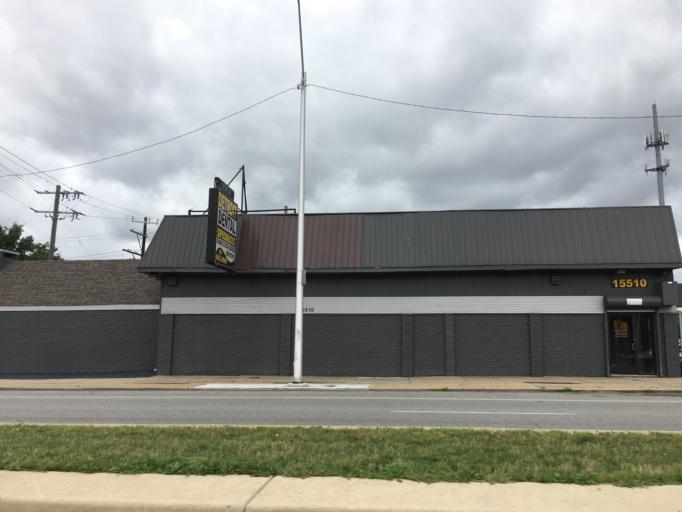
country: US
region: Michigan
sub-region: Wayne County
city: Highland Park
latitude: 42.4060
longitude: -83.1404
